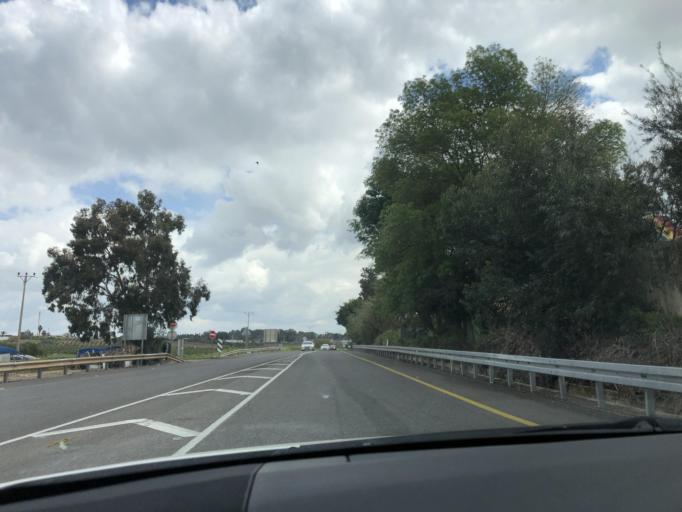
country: IL
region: Central District
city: Tel Mond
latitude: 32.2617
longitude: 34.9177
